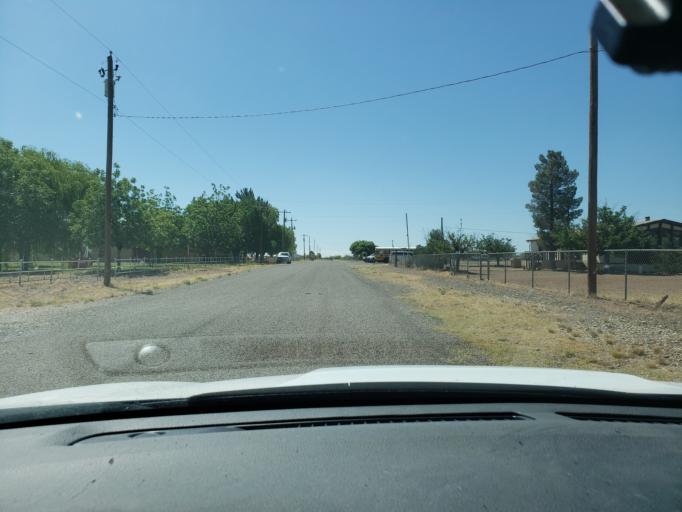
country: US
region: Texas
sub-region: Presidio County
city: Marfa
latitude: 30.5898
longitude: -104.4930
